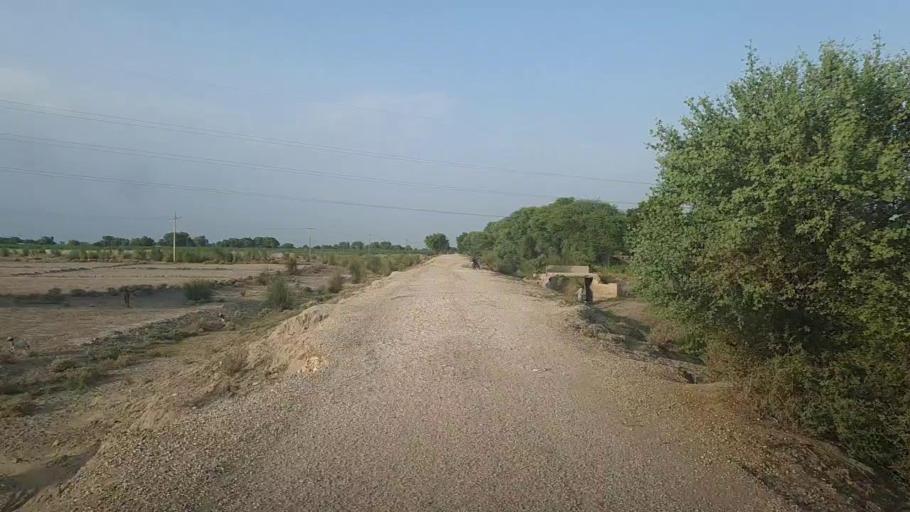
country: PK
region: Sindh
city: Ubauro
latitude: 28.3661
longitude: 69.7954
